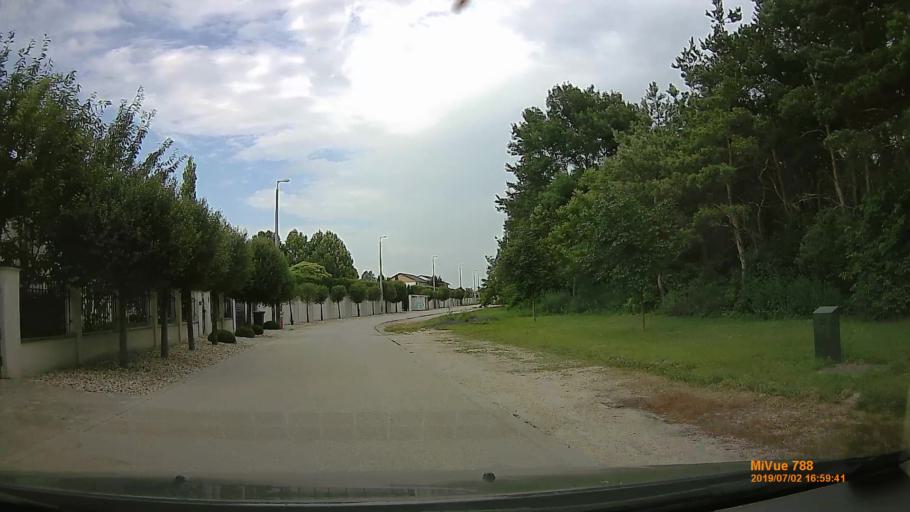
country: HU
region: Gyor-Moson-Sopron
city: Mosonmagyarovar
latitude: 47.8874
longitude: 17.2865
